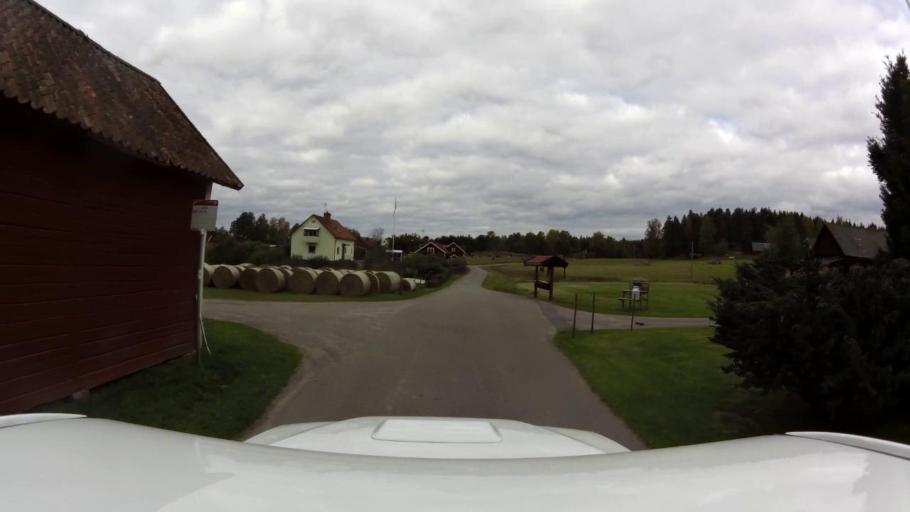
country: SE
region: OEstergoetland
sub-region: Kinda Kommun
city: Rimforsa
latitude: 58.1984
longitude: 15.5771
